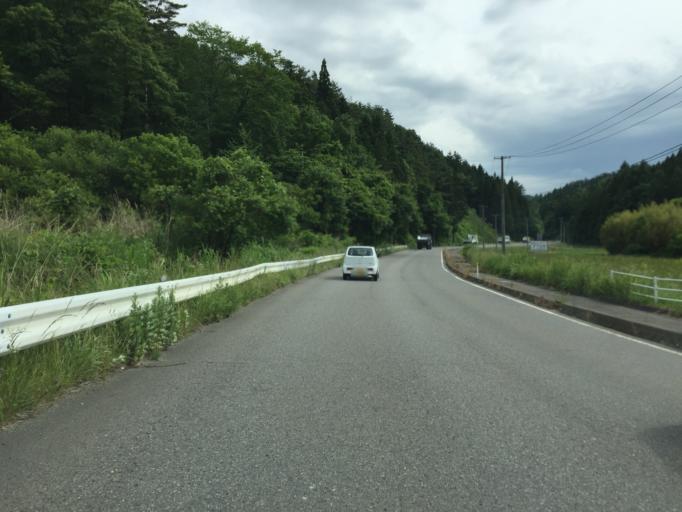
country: JP
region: Fukushima
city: Funehikimachi-funehiki
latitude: 37.4427
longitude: 140.6703
